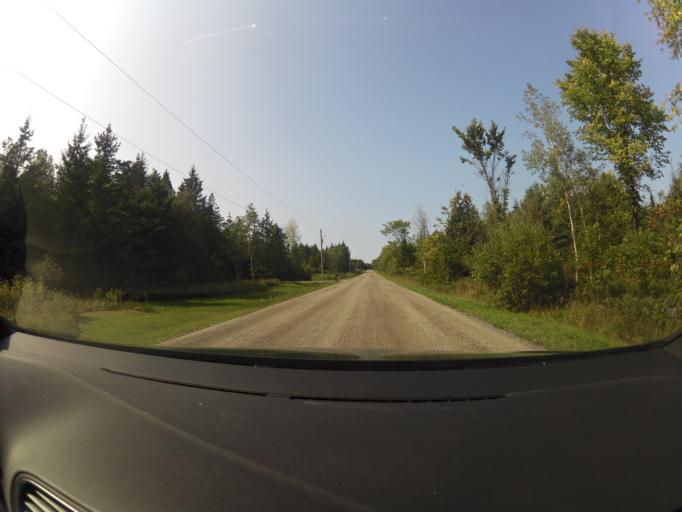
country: CA
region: Ontario
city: Carleton Place
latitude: 45.3192
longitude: -76.1439
